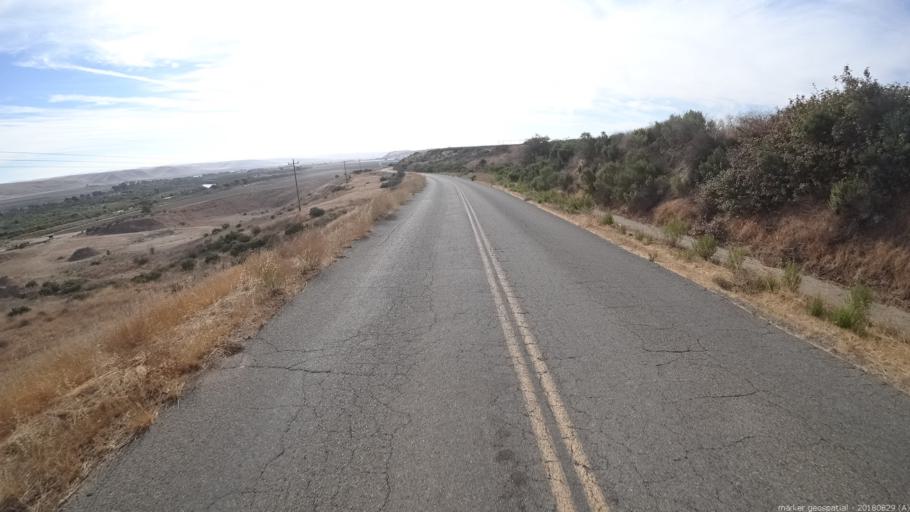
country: US
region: California
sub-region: Monterey County
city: King City
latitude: 36.0953
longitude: -121.0173
